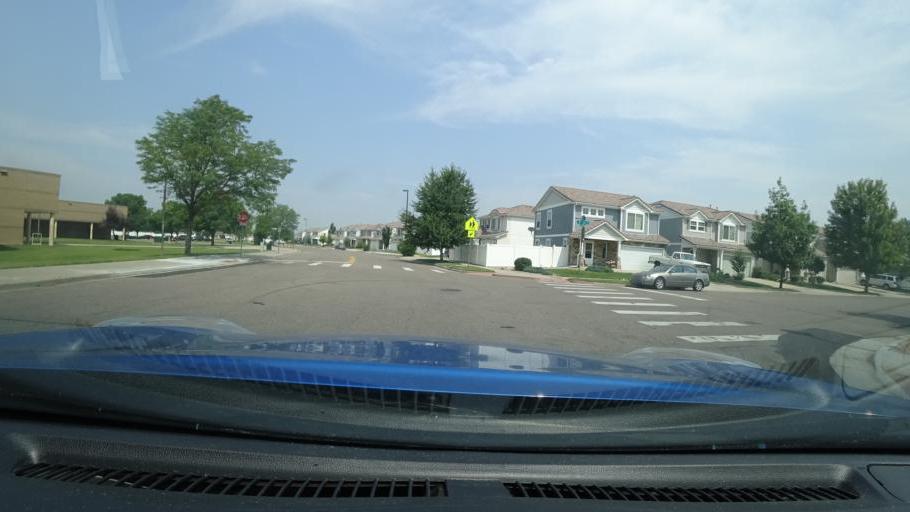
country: US
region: Colorado
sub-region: Adams County
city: Aurora
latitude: 39.7812
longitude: -104.7592
